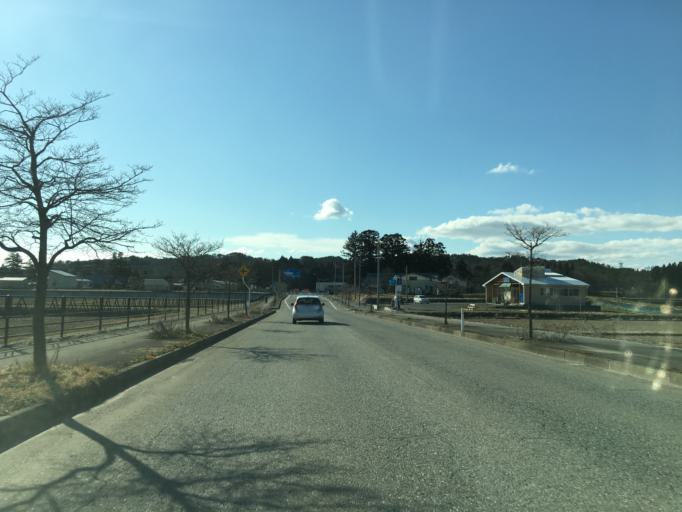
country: JP
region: Yamagata
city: Nagai
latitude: 38.0132
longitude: 140.0451
